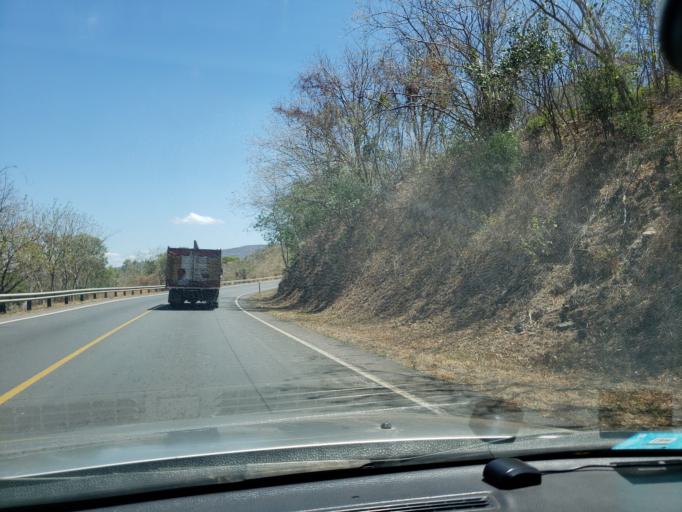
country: NI
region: Boaco
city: Teustepe
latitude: 12.3534
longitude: -85.9135
